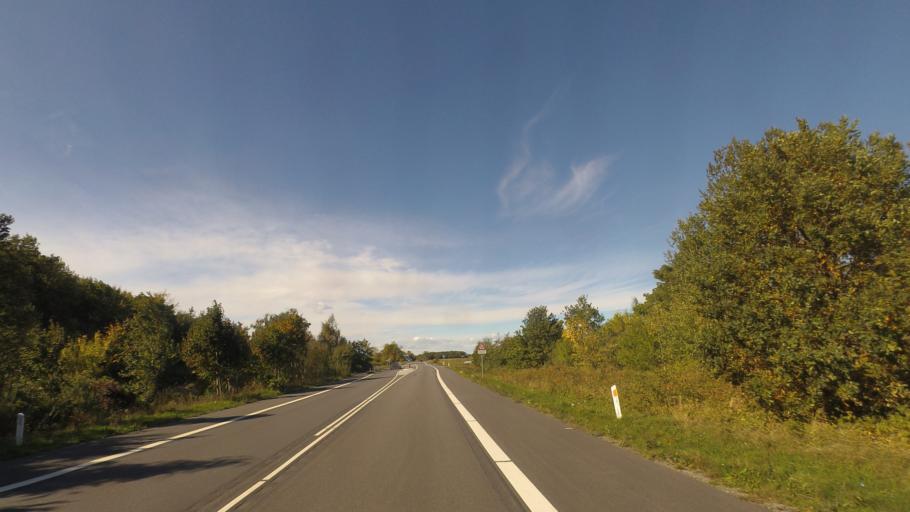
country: DK
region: Capital Region
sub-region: Bornholm Kommune
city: Ronne
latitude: 55.0862
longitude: 14.7458
